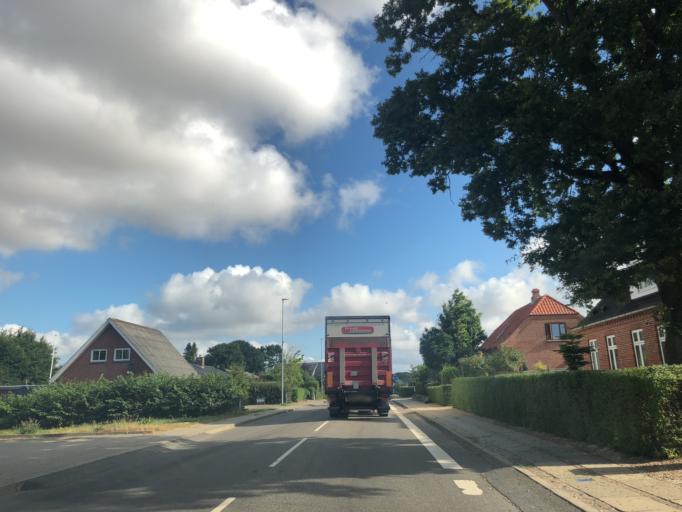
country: DK
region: Central Jutland
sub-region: Skive Kommune
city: Skive
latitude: 56.6523
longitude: 8.9330
